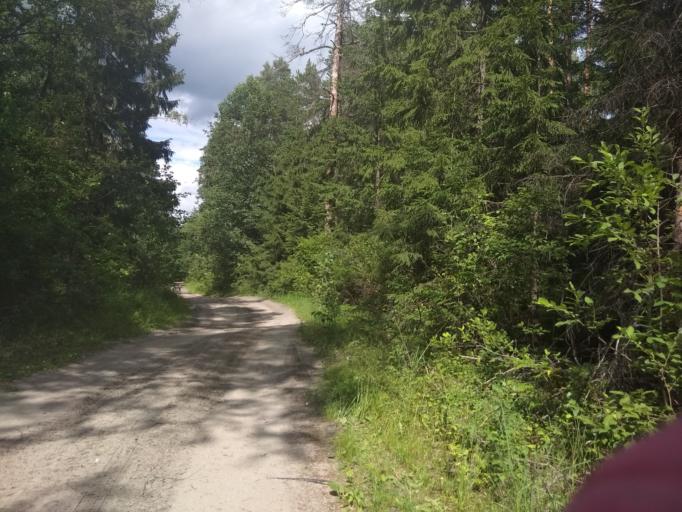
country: RU
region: Moskovskaya
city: Misheronskiy
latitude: 55.7279
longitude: 39.7593
